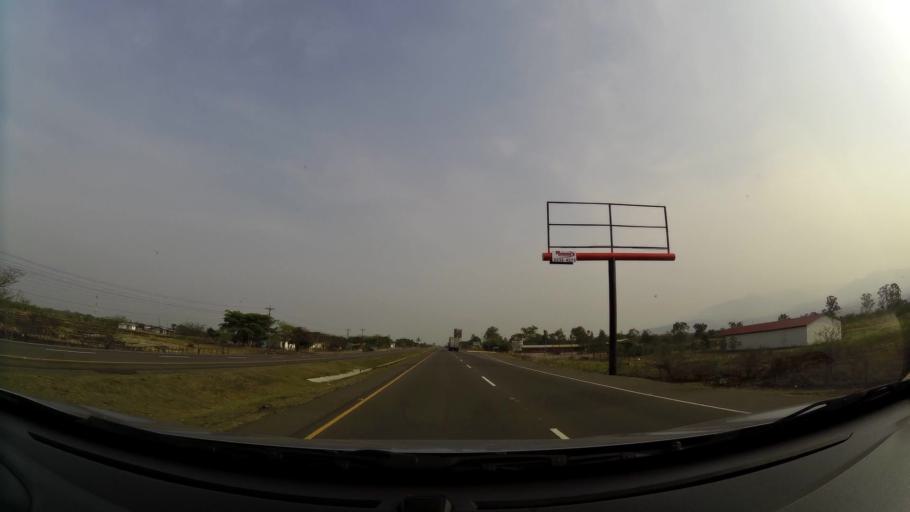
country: HN
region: Comayagua
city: Villa de San Antonio
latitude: 14.3282
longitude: -87.5870
